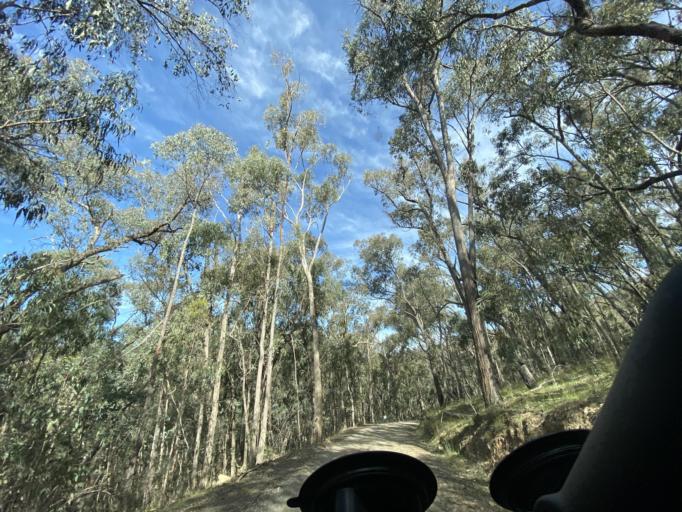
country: AU
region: Victoria
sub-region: Mansfield
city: Mansfield
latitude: -36.8000
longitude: 146.1160
